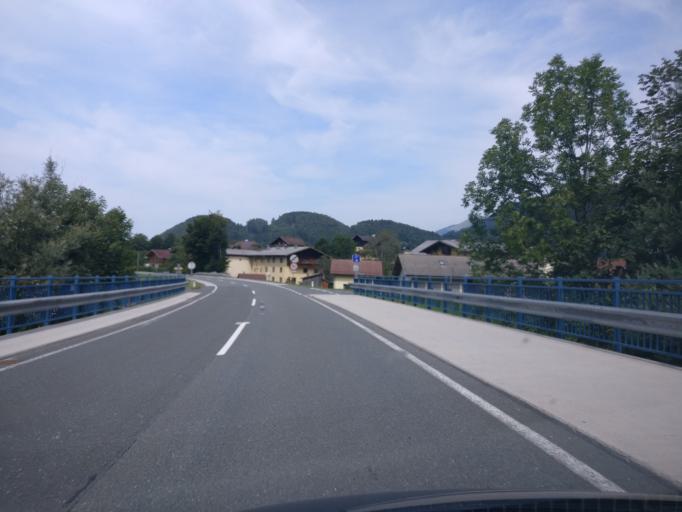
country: AT
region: Salzburg
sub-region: Politischer Bezirk Hallein
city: Golling an der Salzach
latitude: 47.5835
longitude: 13.1824
